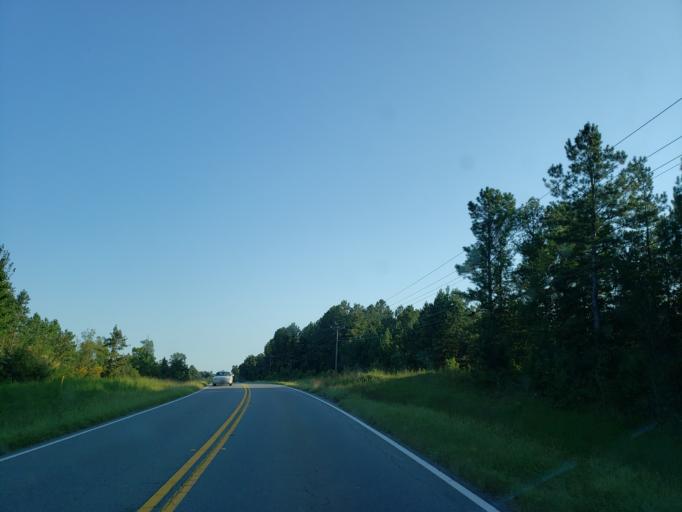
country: US
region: Georgia
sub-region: Murray County
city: Chatsworth
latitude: 34.6958
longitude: -84.8235
